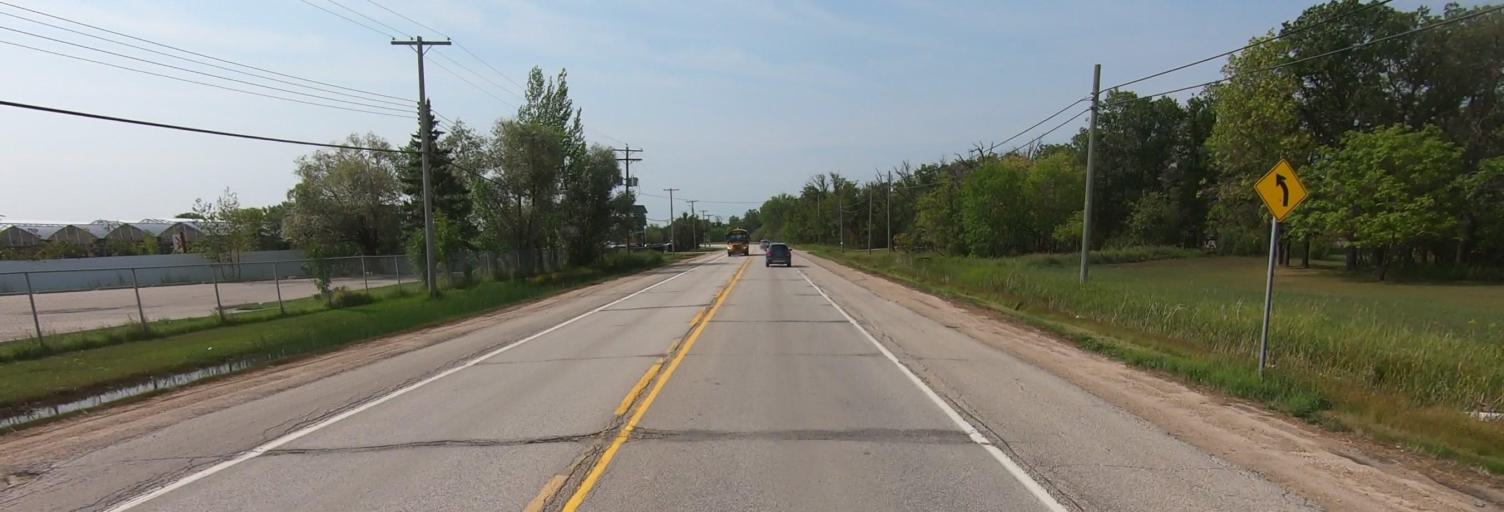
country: CA
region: Manitoba
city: Winnipeg
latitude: 49.7832
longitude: -97.1229
